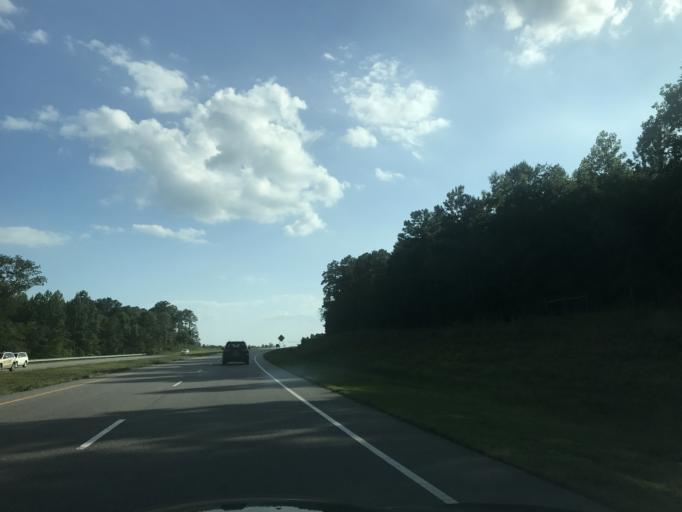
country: US
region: North Carolina
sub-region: Wake County
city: Rolesville
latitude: 35.9189
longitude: -78.4443
